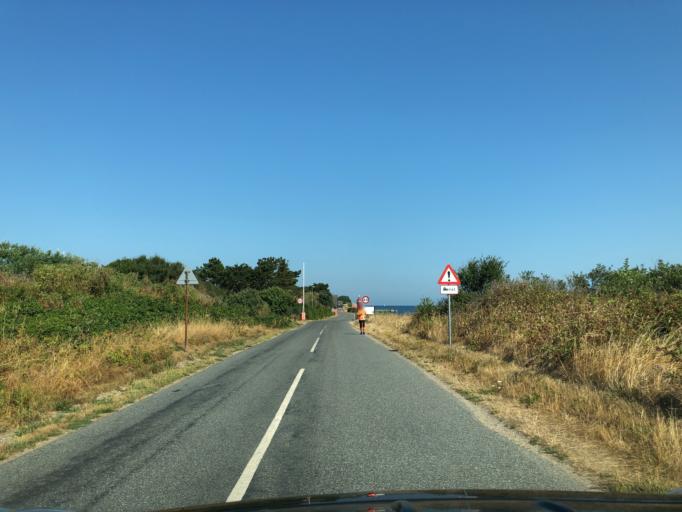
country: DK
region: Zealand
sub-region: Odsherred Kommune
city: Asnaes
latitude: 56.0014
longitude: 11.2866
